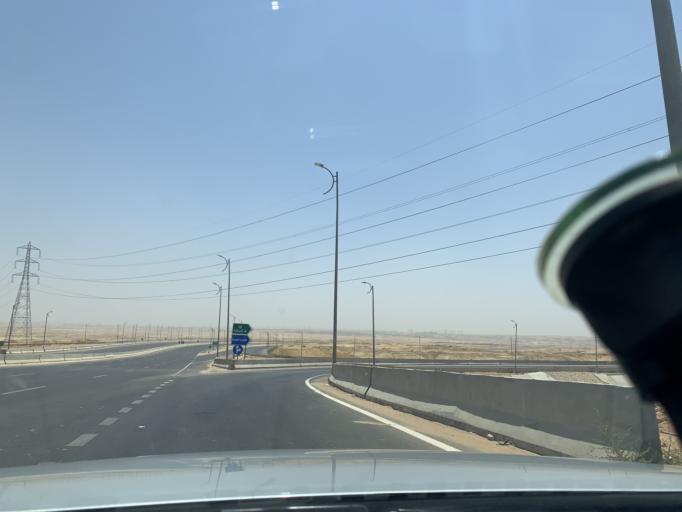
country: EG
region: Muhafazat al Qahirah
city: Halwan
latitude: 29.9661
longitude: 31.4694
